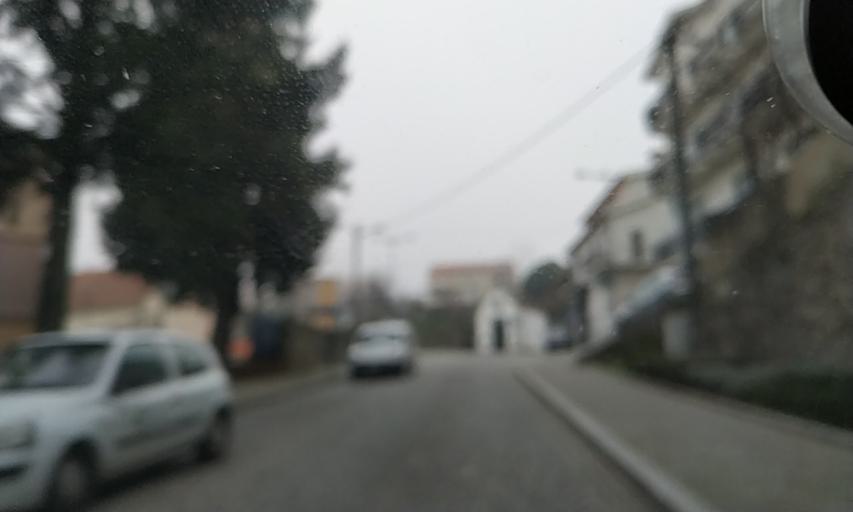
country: PT
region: Viseu
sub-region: Lamego
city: Lamego
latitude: 41.1038
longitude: -7.8099
